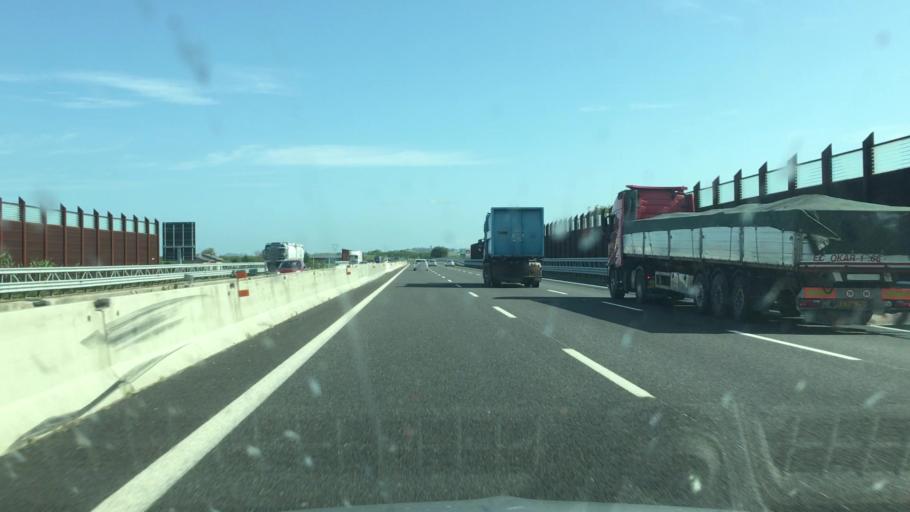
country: IT
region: Emilia-Romagna
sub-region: Provincia di Rimini
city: Coriano
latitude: 44.0053
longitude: 12.6007
